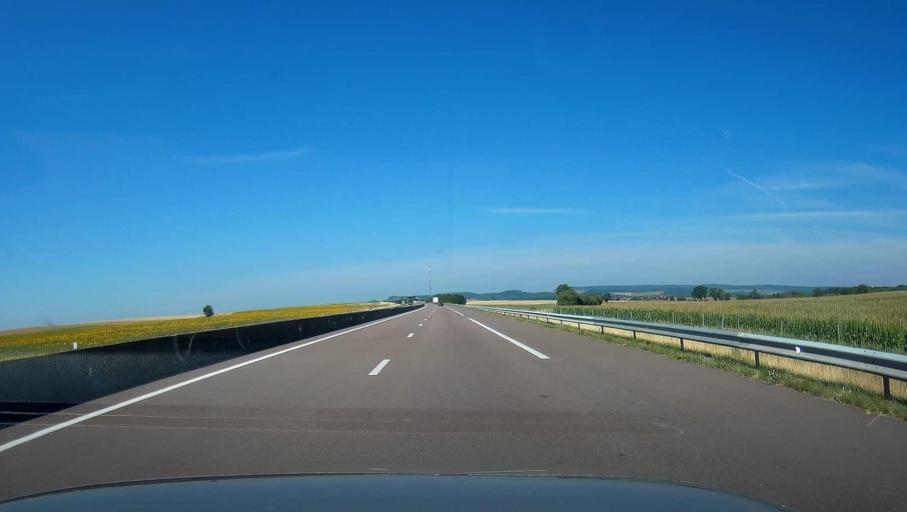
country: FR
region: Lorraine
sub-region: Departement des Vosges
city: Bulgneville
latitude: 48.1791
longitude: 5.7388
